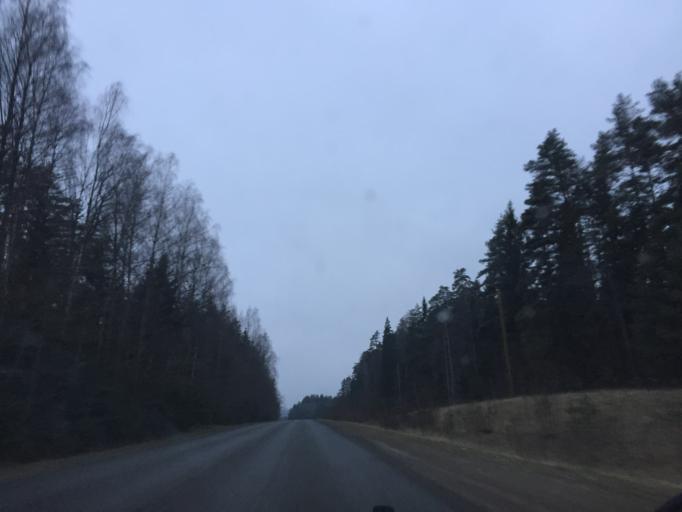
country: LV
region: Priekuli
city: Priekuli
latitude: 57.3254
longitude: 25.4282
